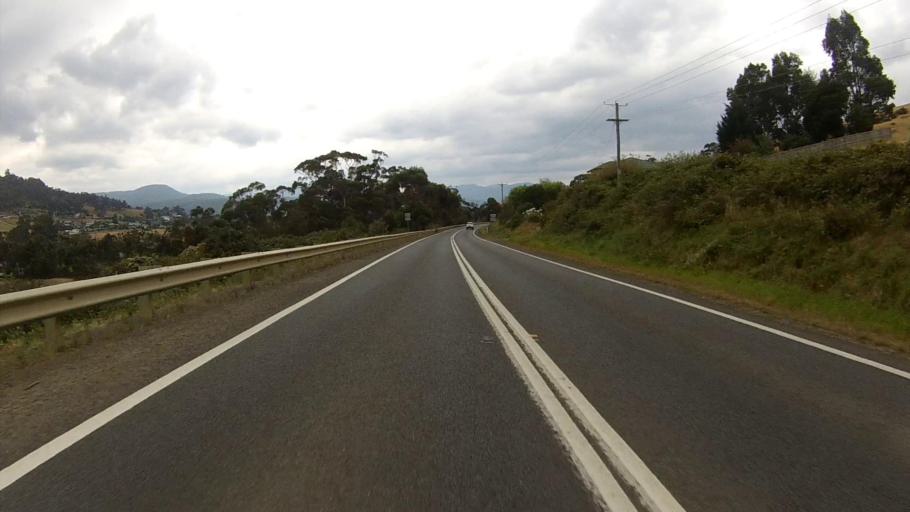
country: AU
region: Tasmania
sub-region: Huon Valley
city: Huonville
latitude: -43.0469
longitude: 147.0509
